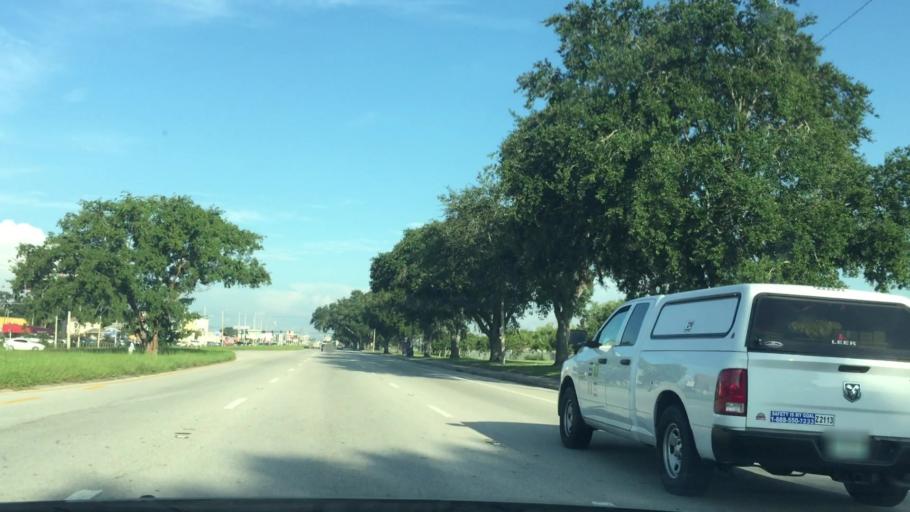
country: US
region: Florida
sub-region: Orange County
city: Pine Hills
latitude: 28.5527
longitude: -81.4345
